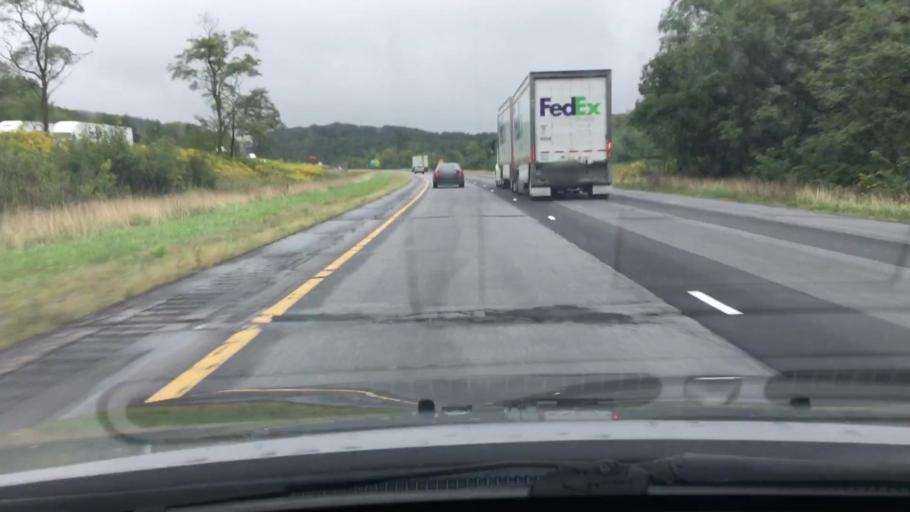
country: US
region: Pennsylvania
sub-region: Lackawanna County
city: Mount Cobb
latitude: 41.3892
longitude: -75.4627
